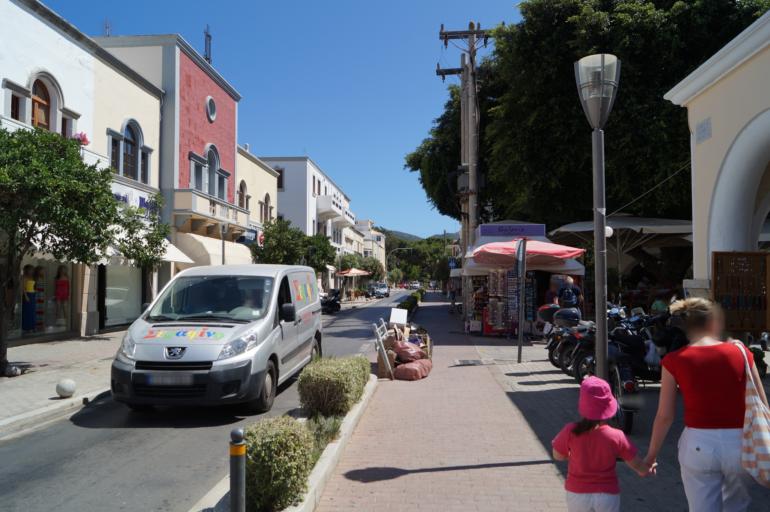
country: GR
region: South Aegean
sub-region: Nomos Dodekanisou
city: Kos
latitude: 36.8928
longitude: 27.2889
